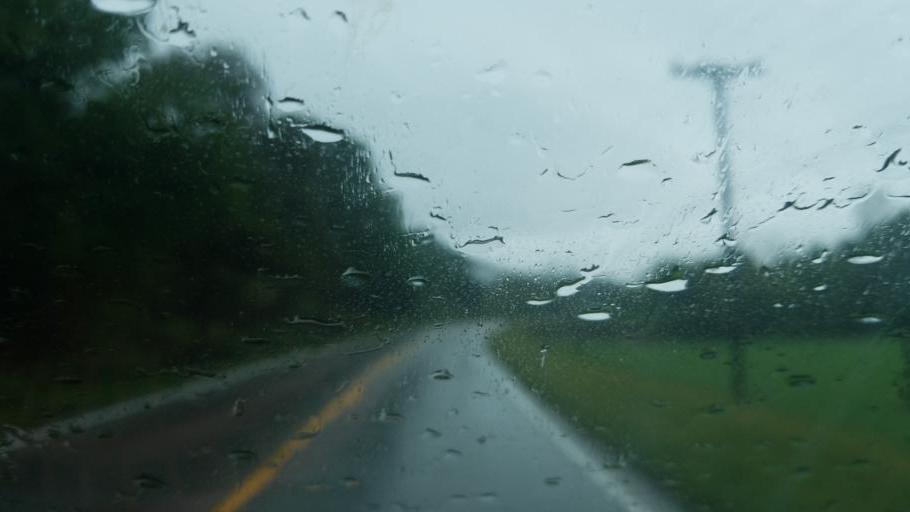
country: US
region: Kentucky
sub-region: Fleming County
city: Flemingsburg
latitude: 38.3477
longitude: -83.6038
